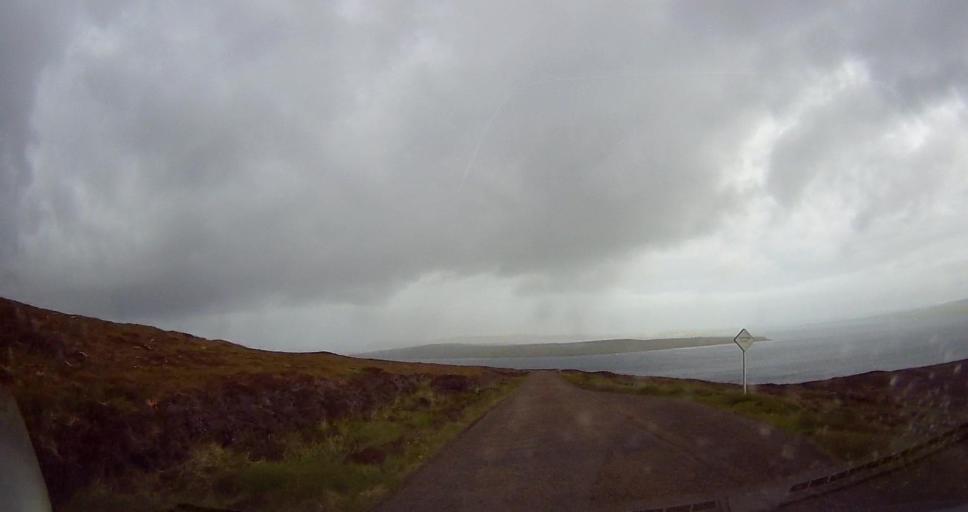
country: GB
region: Scotland
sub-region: Orkney Islands
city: Stromness
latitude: 58.8982
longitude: -3.2738
